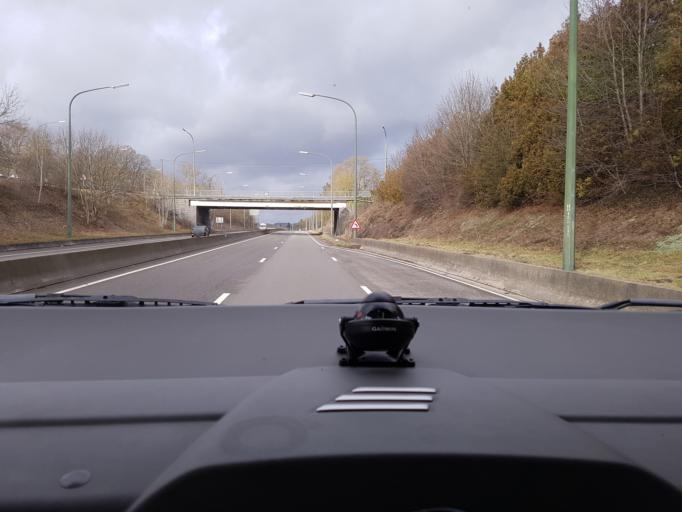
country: BE
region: Wallonia
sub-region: Province du Luxembourg
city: Marche-en-Famenne
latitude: 50.2273
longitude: 5.3339
